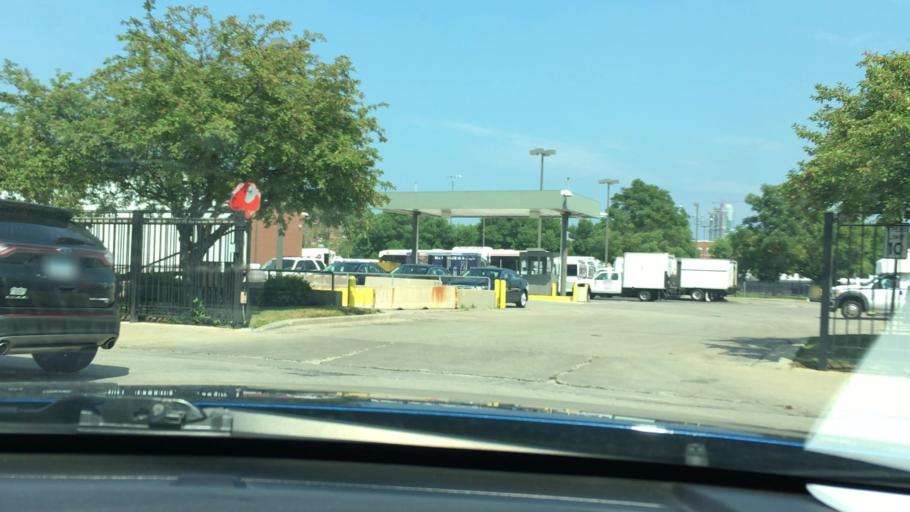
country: US
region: Illinois
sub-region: Cook County
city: Chicago
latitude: 41.8635
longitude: -87.6510
